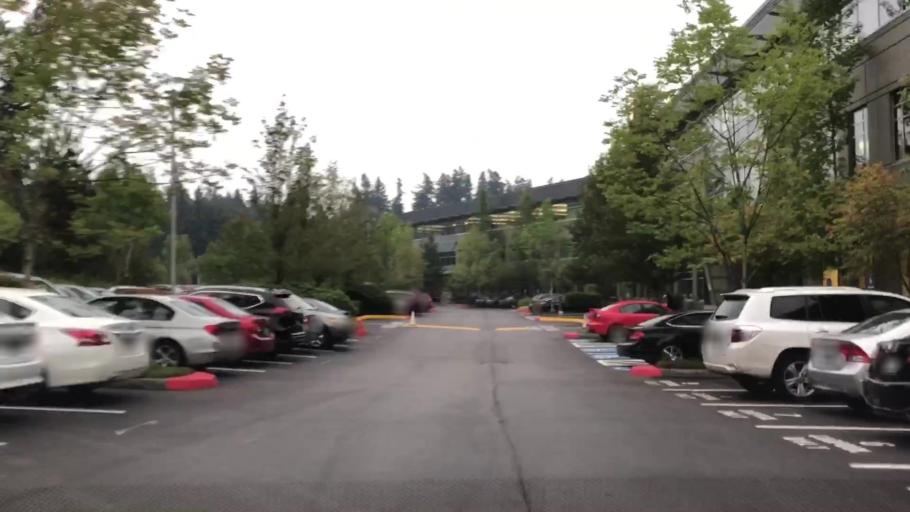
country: US
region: Washington
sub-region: Snohomish County
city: North Creek
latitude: 47.7974
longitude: -122.1948
